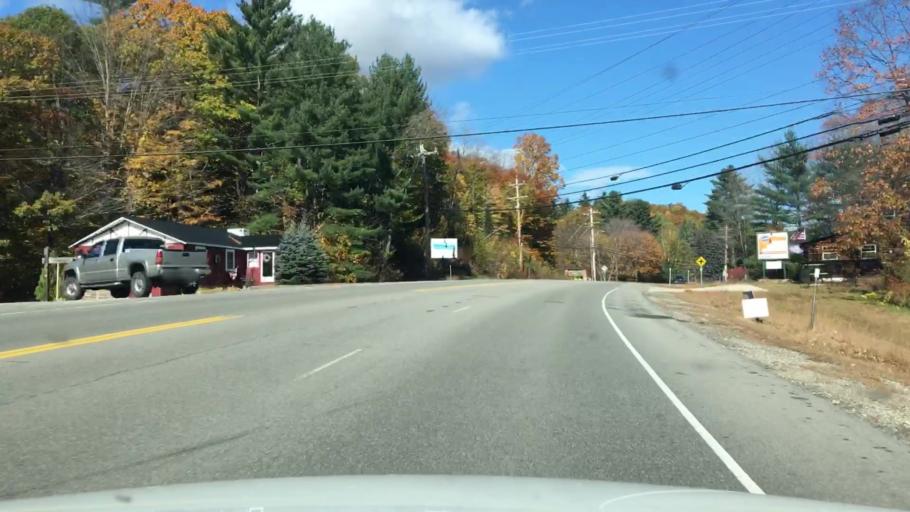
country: US
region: New Hampshire
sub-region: Carroll County
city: North Conway
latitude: 44.1286
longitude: -71.1895
